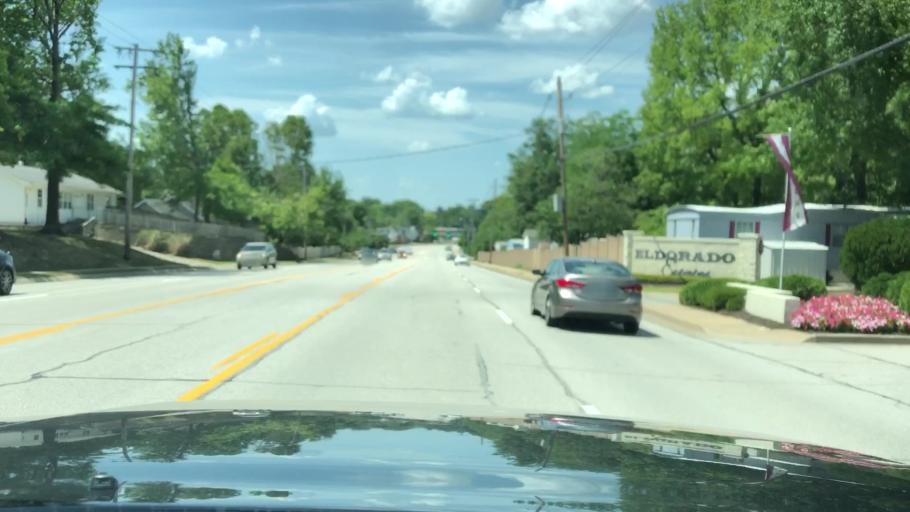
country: US
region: Missouri
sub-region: Saint Charles County
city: Saint Peters
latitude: 38.7894
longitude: -90.6091
